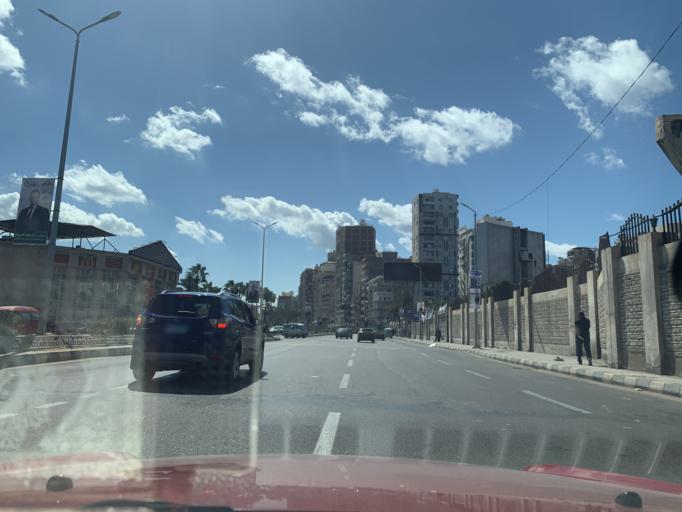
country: EG
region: Alexandria
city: Alexandria
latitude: 31.2195
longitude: 29.9475
